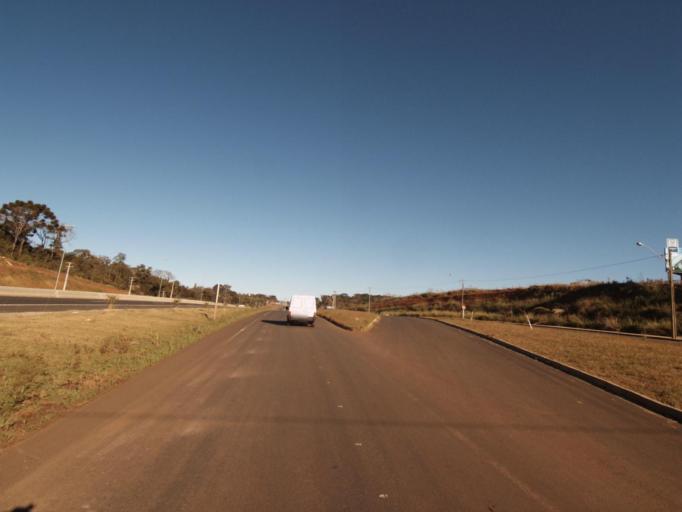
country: BR
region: Santa Catarina
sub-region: Chapeco
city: Chapeco
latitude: -27.0127
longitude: -52.6392
